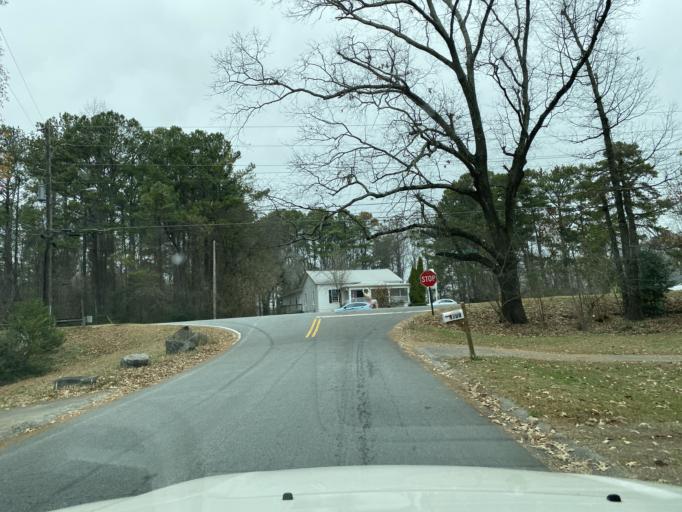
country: US
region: Georgia
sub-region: Cobb County
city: Fair Oaks
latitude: 33.9166
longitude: -84.5850
